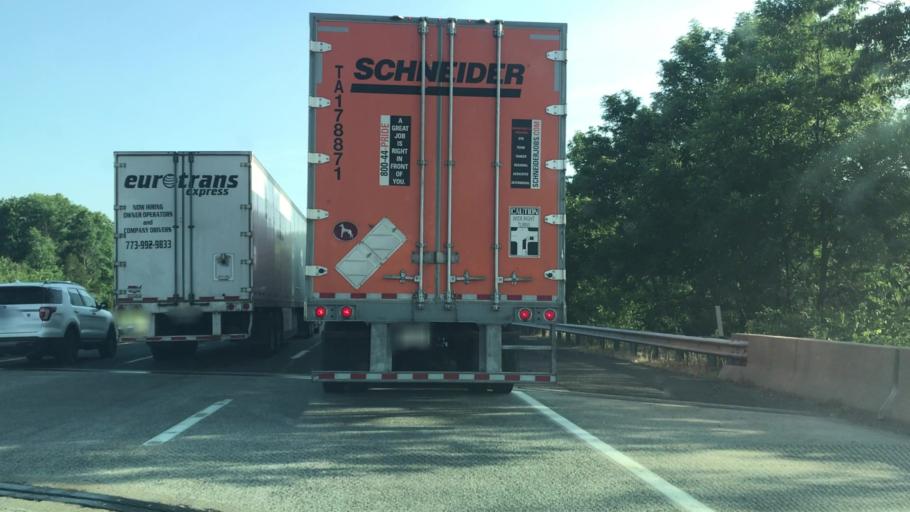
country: US
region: New Jersey
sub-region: Somerset County
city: Bedminster
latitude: 40.6575
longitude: -74.6462
